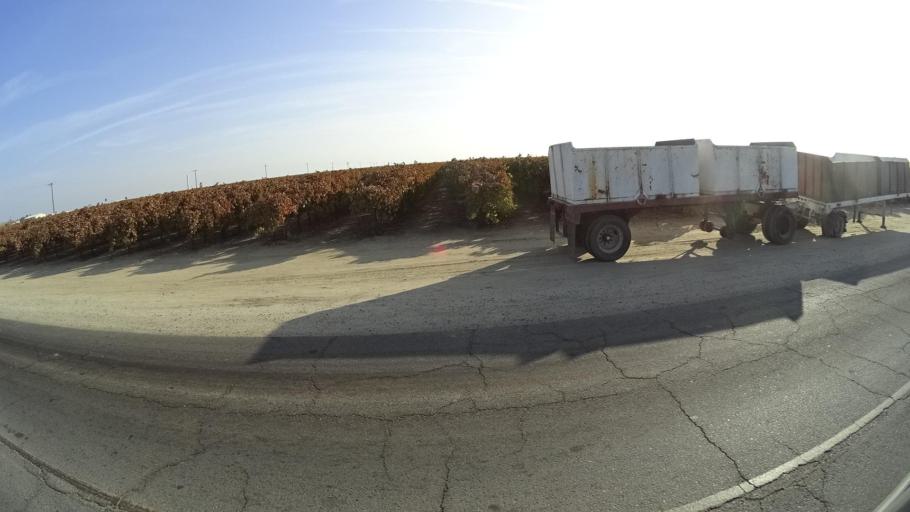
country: US
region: California
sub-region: Kern County
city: Delano
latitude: 35.7897
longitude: -119.1875
